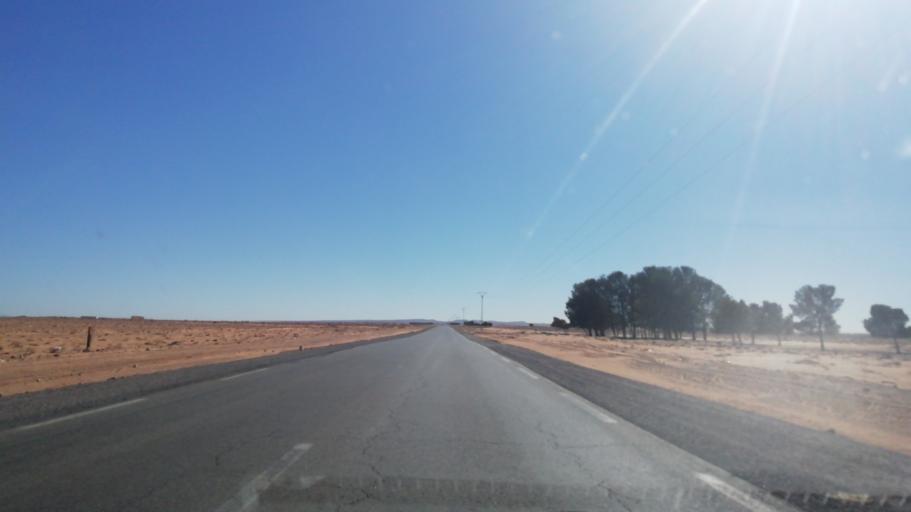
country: DZ
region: Saida
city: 'Ain el Hadjar
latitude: 34.0072
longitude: 0.1224
